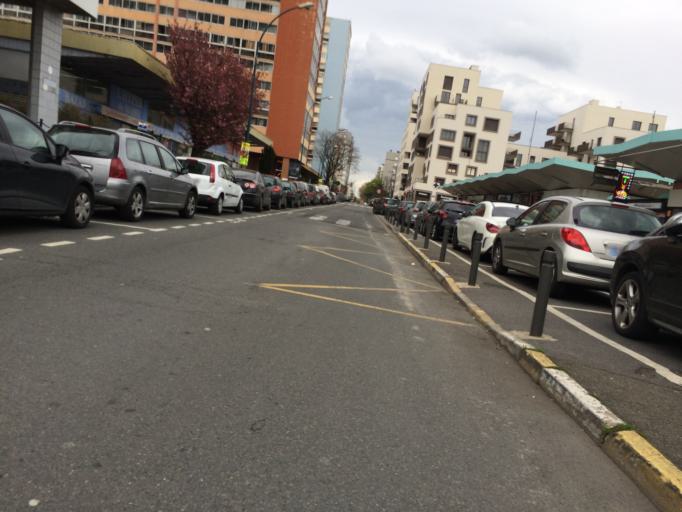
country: FR
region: Ile-de-France
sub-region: Departement de l'Essonne
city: Massy
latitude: 48.7330
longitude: 2.2867
